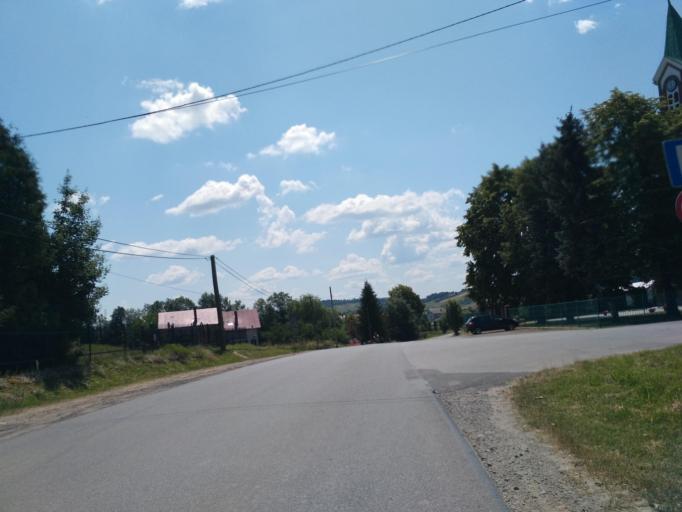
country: PL
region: Subcarpathian Voivodeship
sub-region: Powiat sanocki
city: Niebieszczany
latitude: 49.5073
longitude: 22.1549
